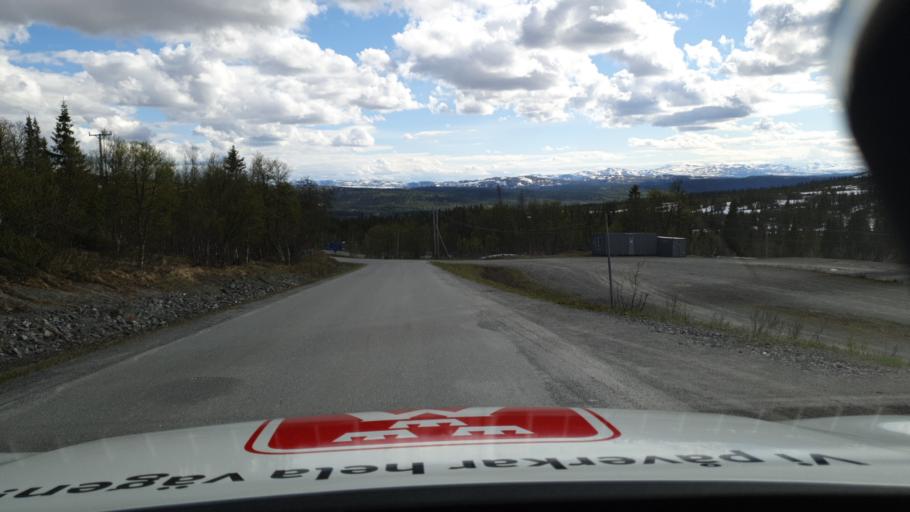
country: SE
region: Jaemtland
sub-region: Are Kommun
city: Are
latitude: 63.4288
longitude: 13.0162
